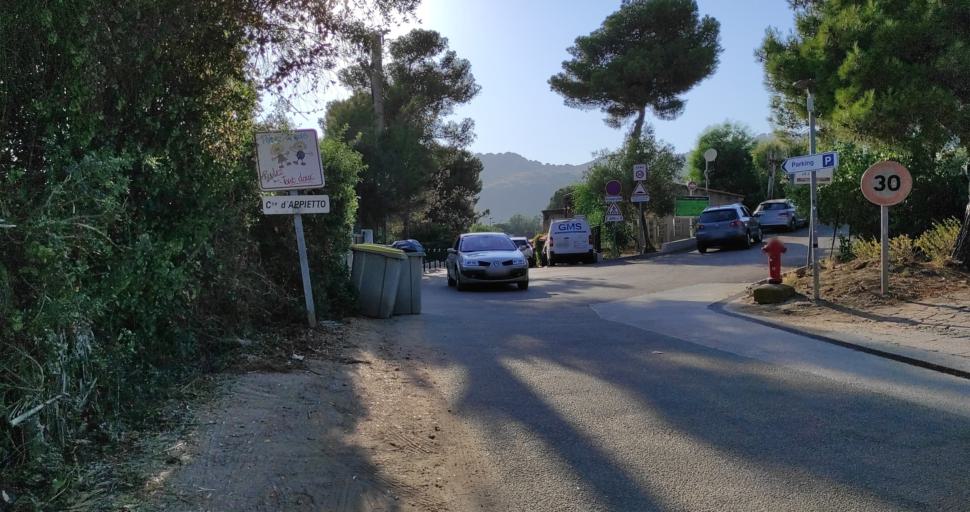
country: FR
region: Corsica
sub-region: Departement de la Corse-du-Sud
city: Alata
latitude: 41.9922
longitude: 8.6725
